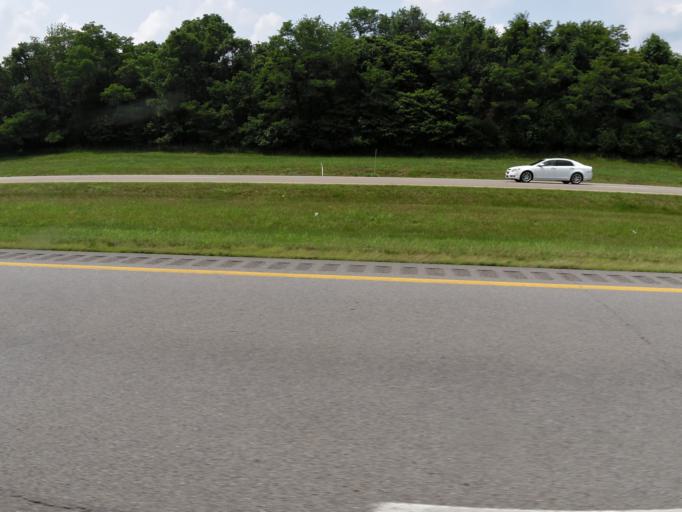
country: US
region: Kentucky
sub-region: Gallatin County
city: Warsaw
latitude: 38.6863
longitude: -84.9511
